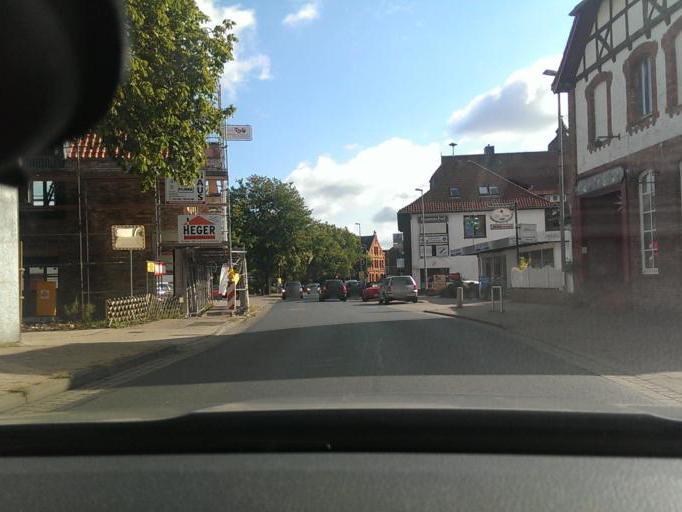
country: DE
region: Lower Saxony
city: Isernhagen Farster Bauerschaft
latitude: 52.4914
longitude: 9.8528
